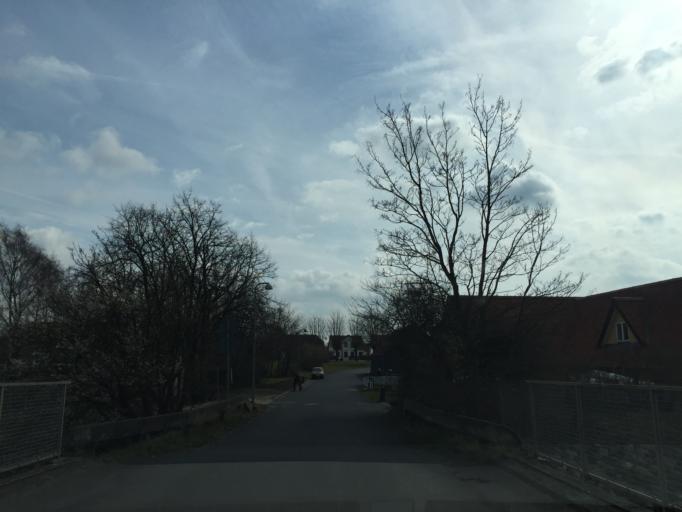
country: DK
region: South Denmark
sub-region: Odense Kommune
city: Stige
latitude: 55.4284
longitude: 10.4143
